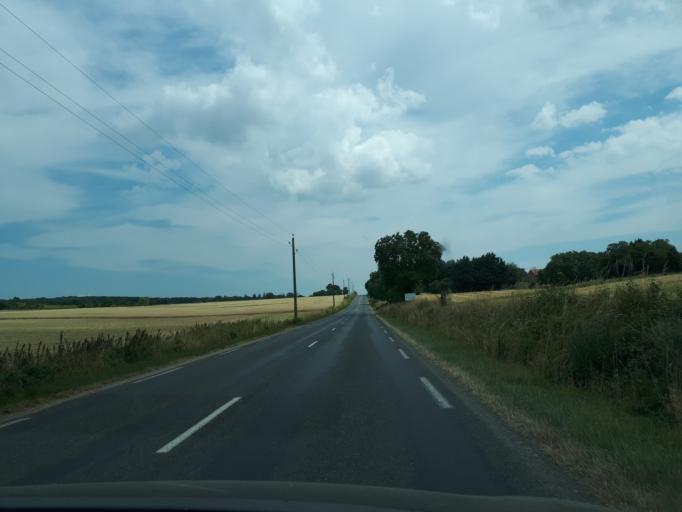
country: FR
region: Centre
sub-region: Departement du Cher
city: Rians
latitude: 47.2160
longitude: 2.6191
